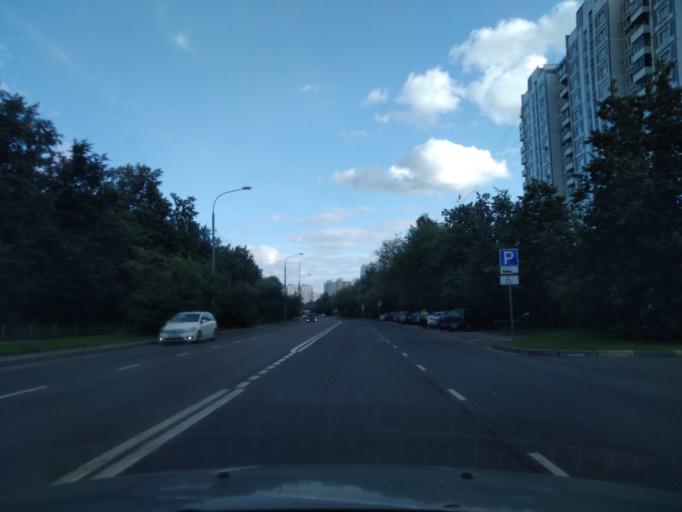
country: RU
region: Moscow
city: Strogino
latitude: 55.8121
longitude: 37.4113
